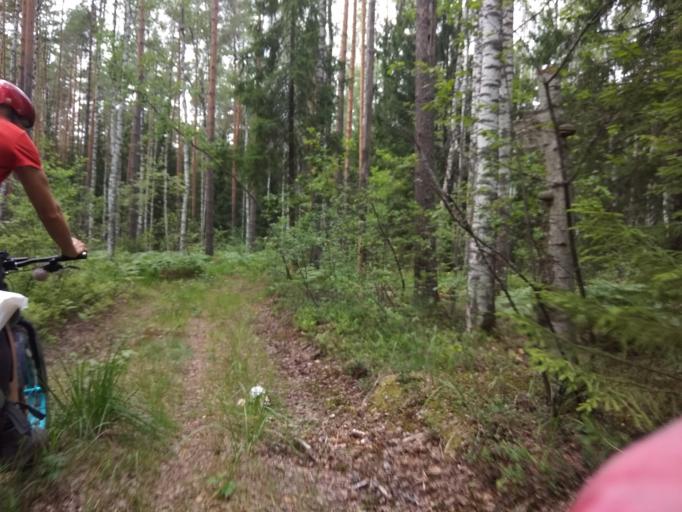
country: RU
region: Moskovskaya
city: Misheronskiy
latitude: 55.6854
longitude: 39.7107
